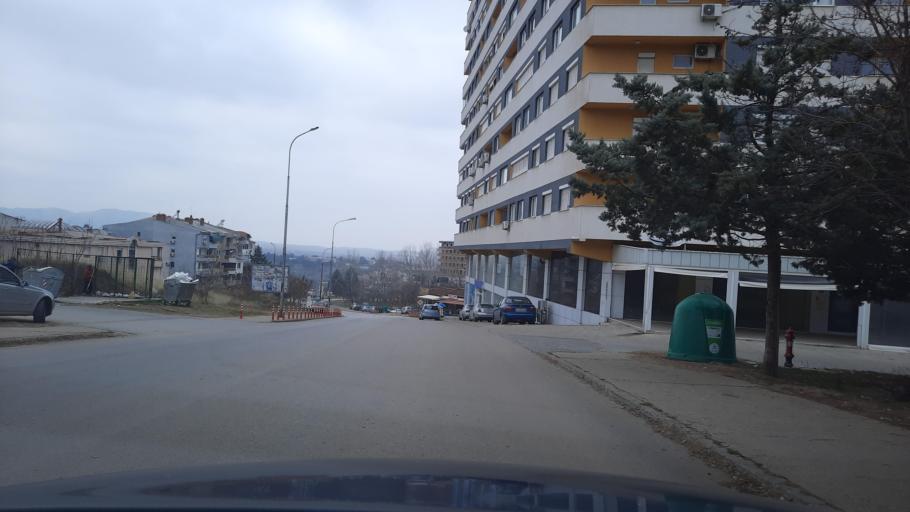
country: MK
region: Stip
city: Shtip
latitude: 41.7493
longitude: 22.2011
